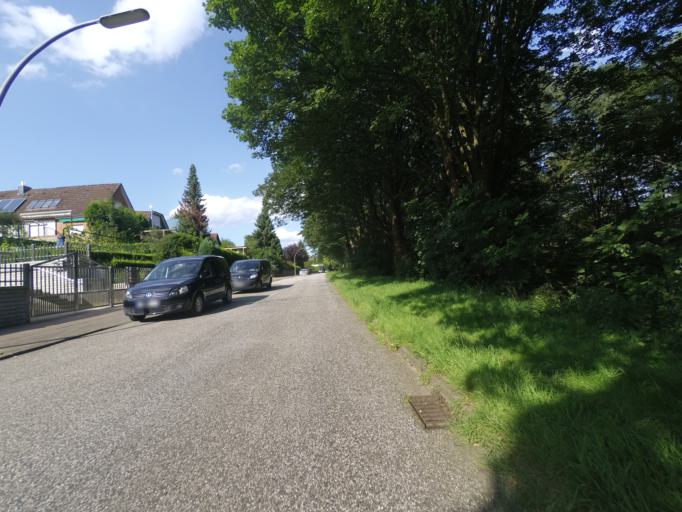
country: DE
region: Schleswig-Holstein
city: Oststeinbek
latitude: 53.5323
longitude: 10.1324
